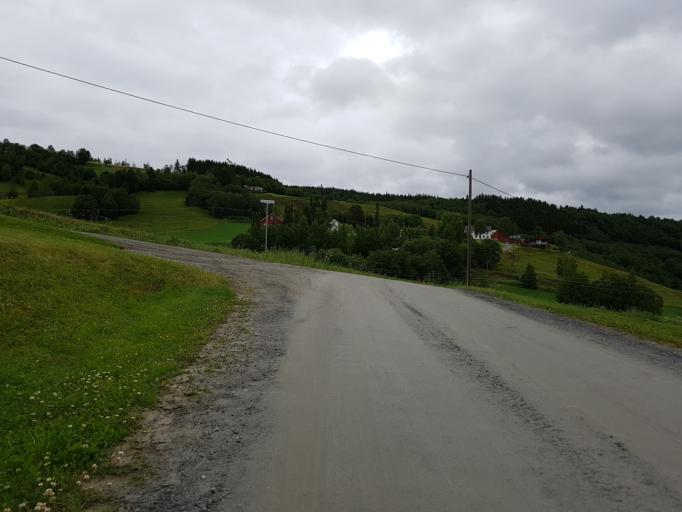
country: NO
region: Sor-Trondelag
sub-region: Selbu
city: Mebonden
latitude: 63.2224
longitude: 11.0397
